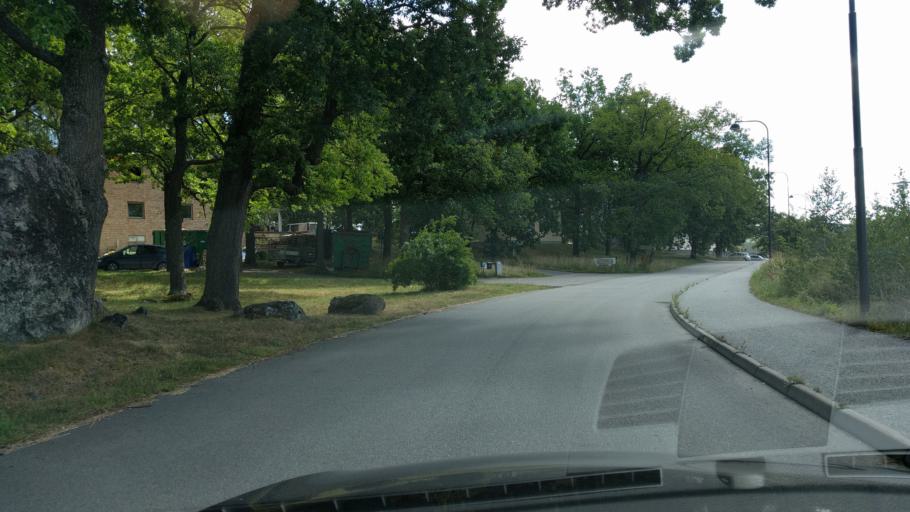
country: SE
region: Stockholm
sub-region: Jarfalla Kommun
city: Jakobsberg
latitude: 59.4191
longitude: 17.8593
